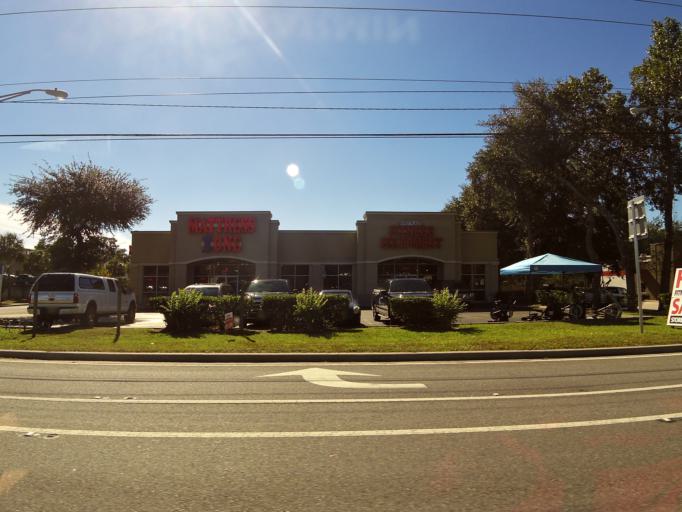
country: US
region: Florida
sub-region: Saint Johns County
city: Fruit Cove
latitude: 30.1815
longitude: -81.5550
